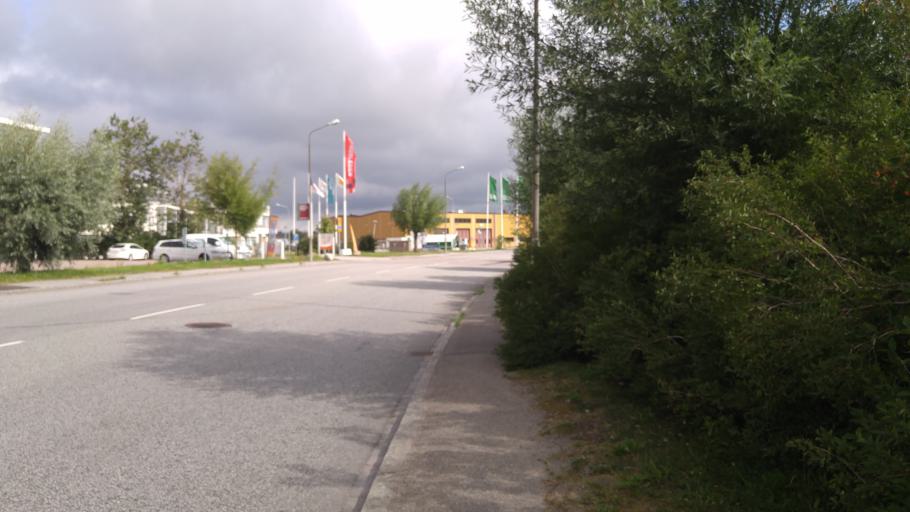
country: SE
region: Skane
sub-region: Malmo
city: Oxie
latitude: 55.5566
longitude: 13.0464
